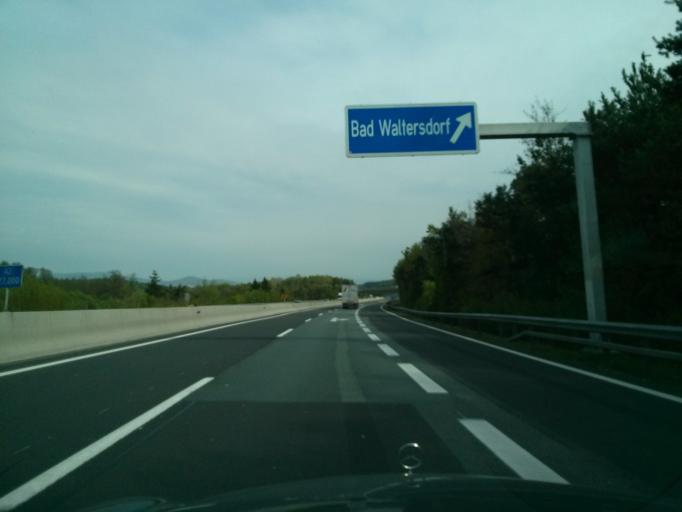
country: AT
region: Styria
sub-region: Politischer Bezirk Hartberg-Fuerstenfeld
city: Bad Waltersdorf
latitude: 47.1763
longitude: 15.9970
